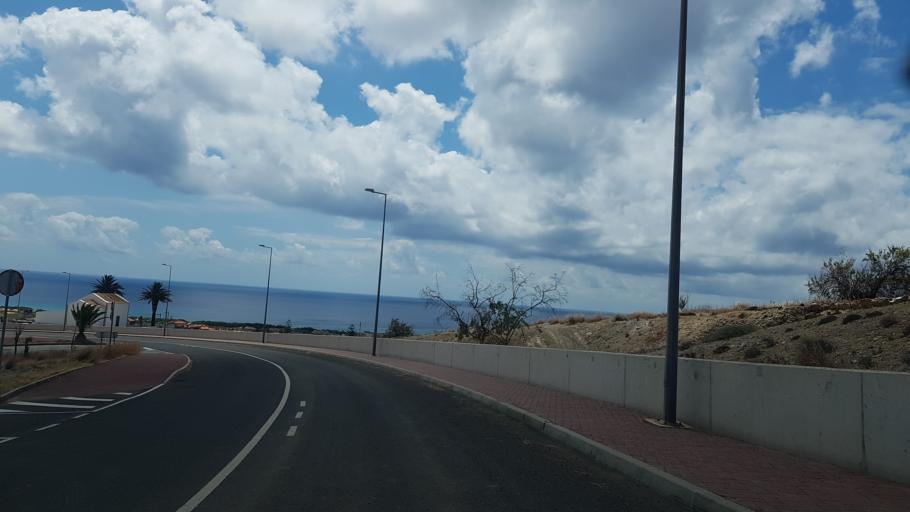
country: PT
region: Madeira
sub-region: Porto Santo
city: Vila de Porto Santo
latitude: 33.0462
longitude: -16.3642
